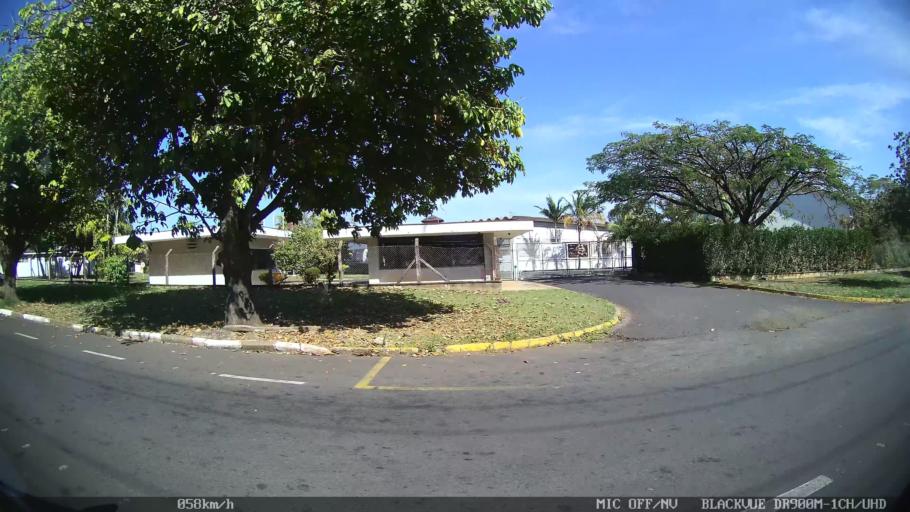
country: BR
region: Sao Paulo
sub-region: Franca
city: Franca
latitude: -20.5518
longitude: -47.4466
